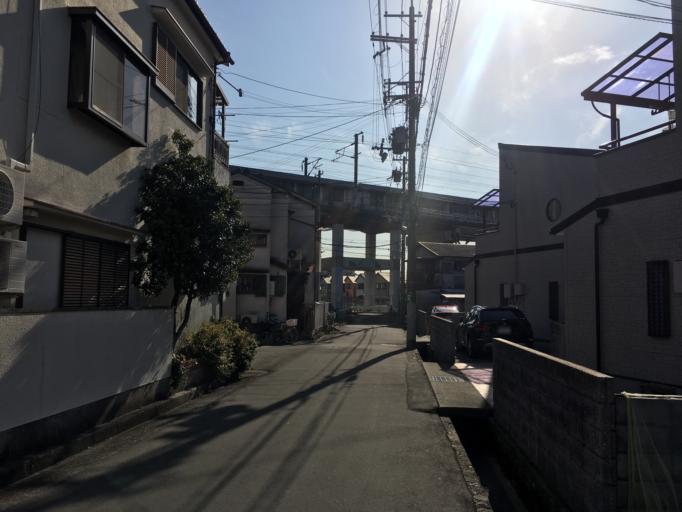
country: JP
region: Hyogo
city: Takarazuka
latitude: 34.7660
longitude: 135.3684
